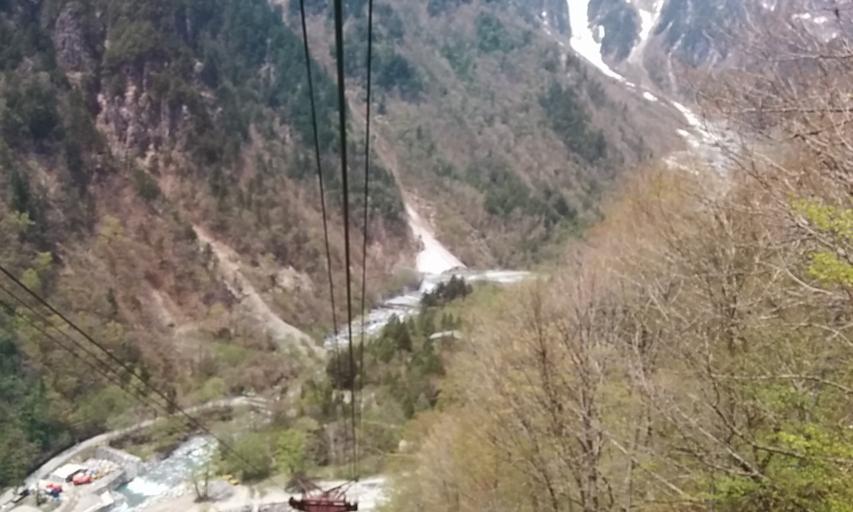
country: JP
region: Nagano
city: Hotaka
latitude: 36.2846
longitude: 137.5774
